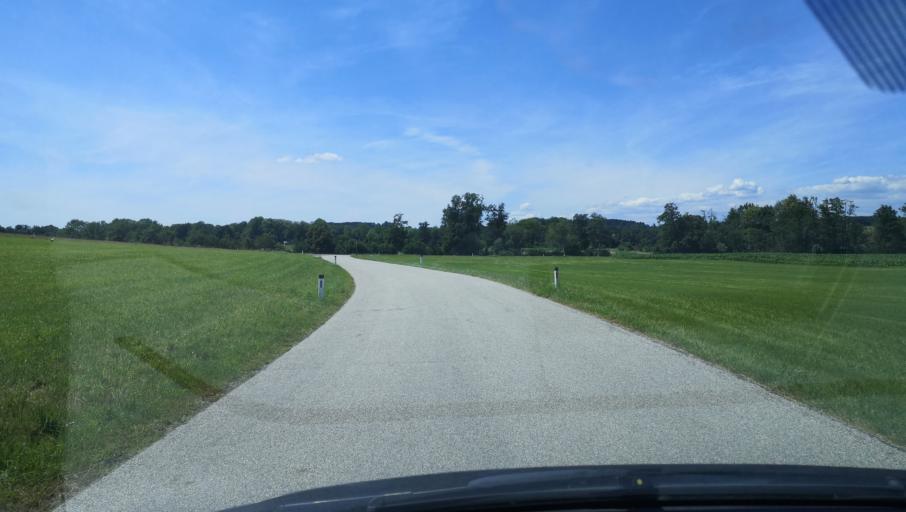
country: AT
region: Lower Austria
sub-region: Politischer Bezirk Amstetten
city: Euratsfeld
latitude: 48.0748
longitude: 14.9038
